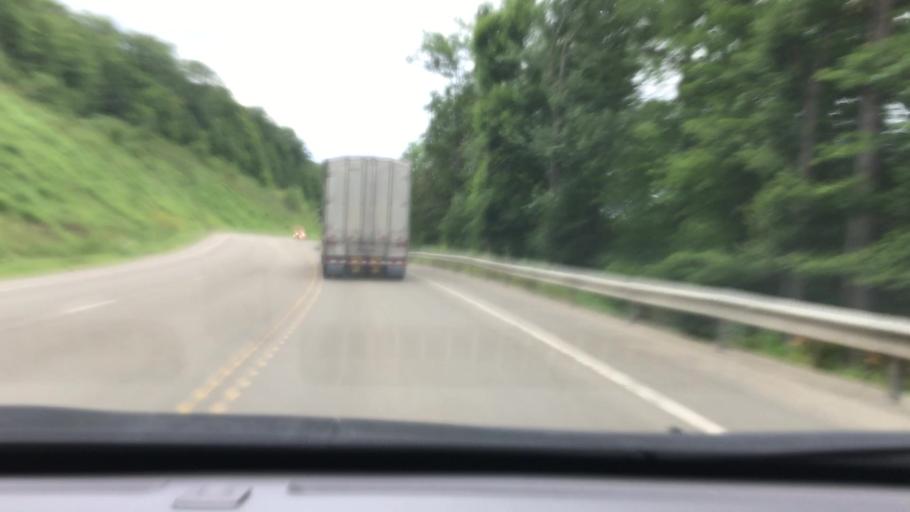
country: US
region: Pennsylvania
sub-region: McKean County
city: Kane
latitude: 41.7498
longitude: -78.6892
